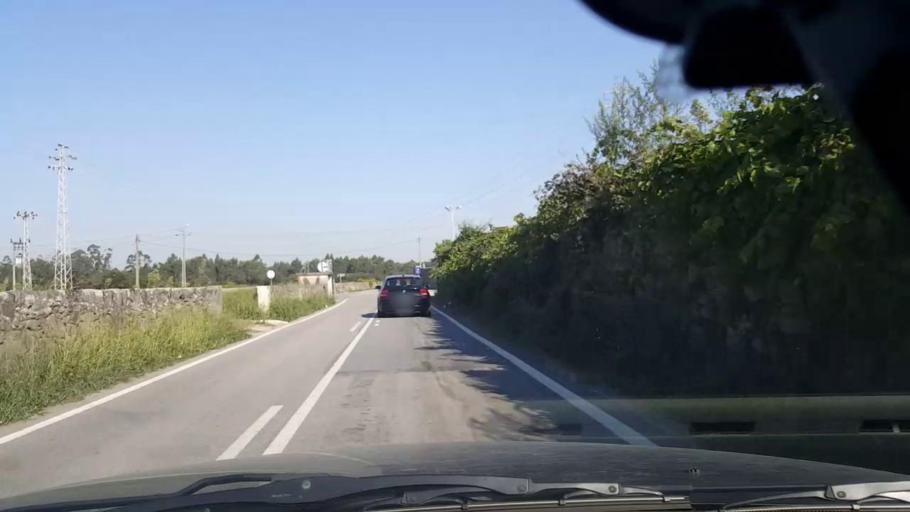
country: PT
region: Porto
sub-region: Vila do Conde
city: Arvore
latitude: 41.3252
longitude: -8.6814
